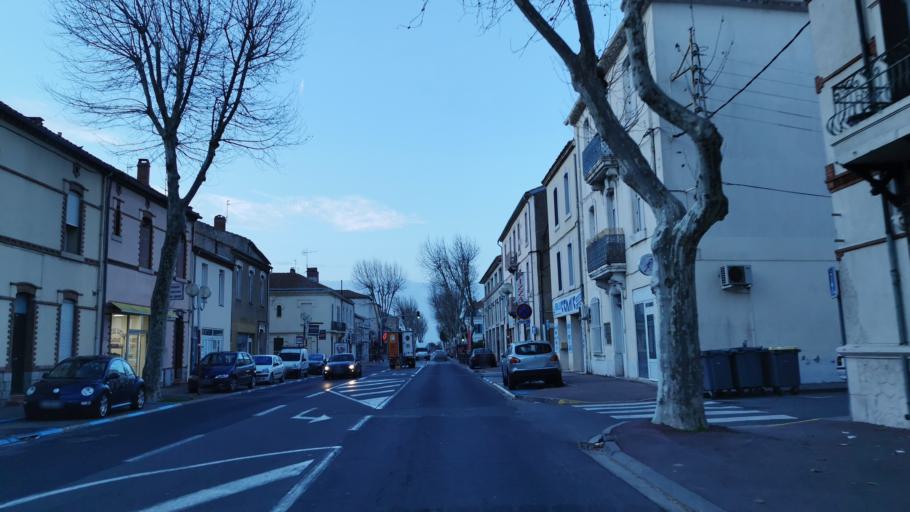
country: FR
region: Languedoc-Roussillon
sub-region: Departement de l'Aude
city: Narbonne
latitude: 43.1801
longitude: 2.9964
